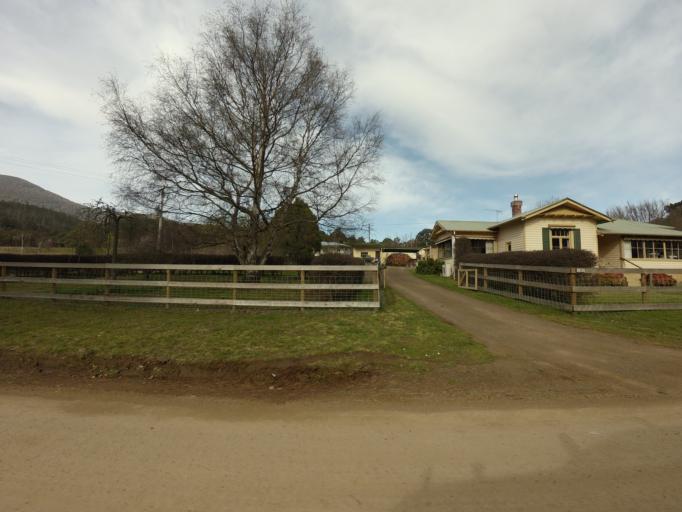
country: AU
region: Tasmania
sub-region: Huon Valley
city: Huonville
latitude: -43.0758
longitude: 147.0699
